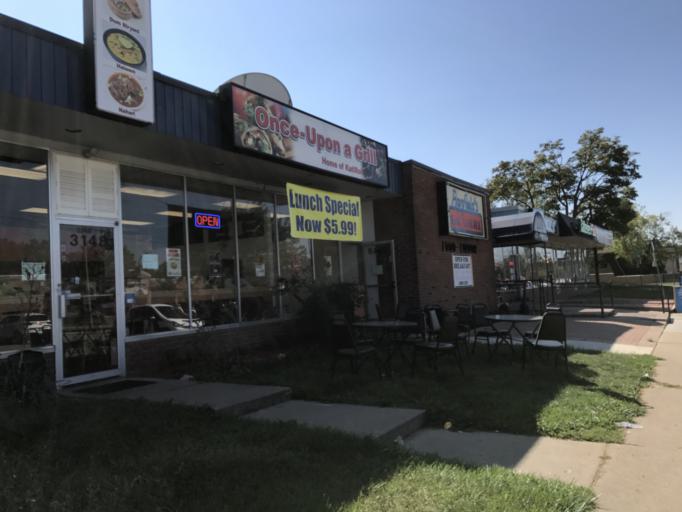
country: US
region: Michigan
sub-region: Washtenaw County
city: Ann Arbor
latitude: 42.2448
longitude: -83.6973
